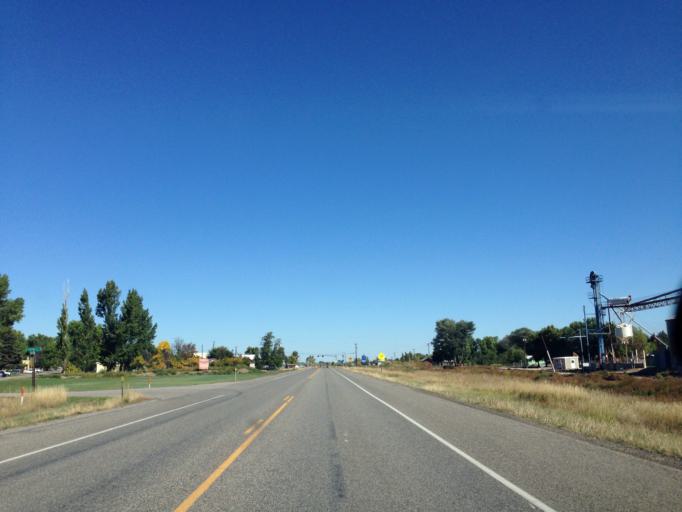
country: US
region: Montana
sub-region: Yellowstone County
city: Laurel
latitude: 45.3886
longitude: -108.9089
